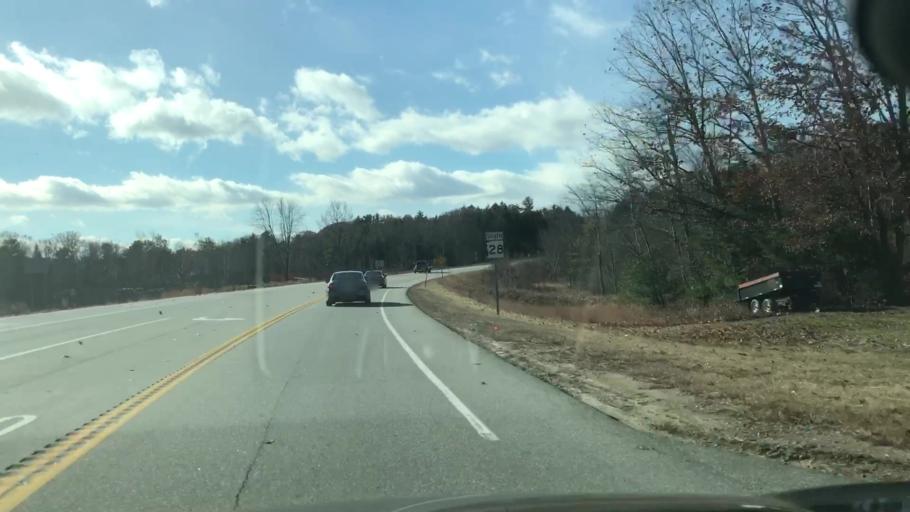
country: US
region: New Hampshire
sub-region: Belknap County
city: Barnstead
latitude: 43.3444
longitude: -71.2678
